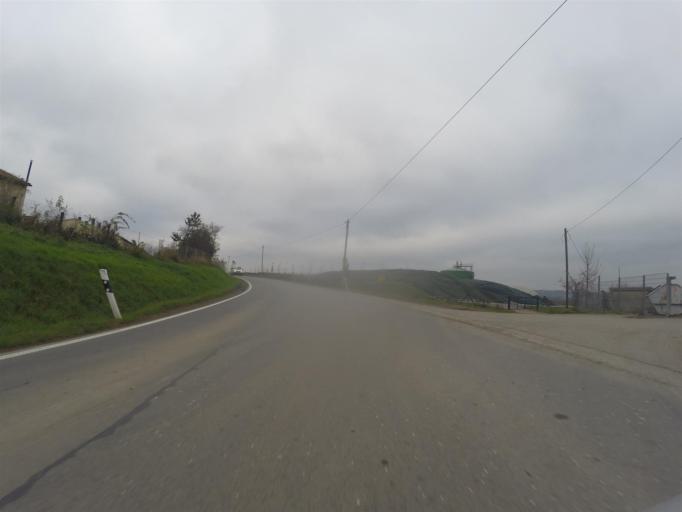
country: DE
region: Thuringia
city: Schongleina
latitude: 50.9212
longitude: 11.7317
